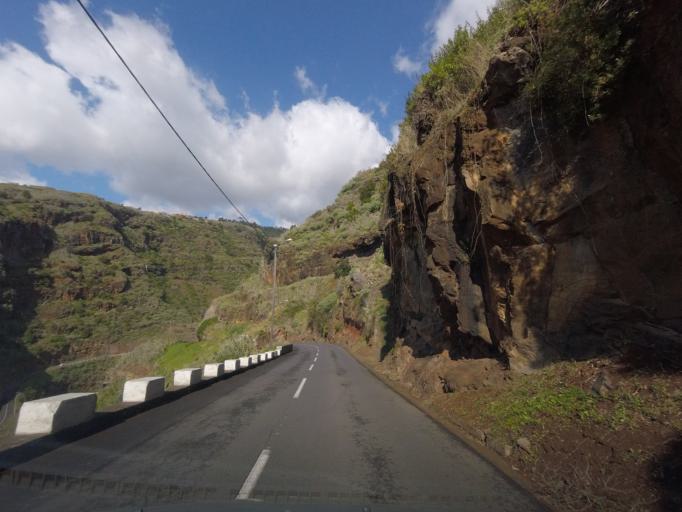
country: PT
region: Madeira
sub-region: Calheta
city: Estreito da Calheta
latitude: 32.7339
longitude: -17.1987
